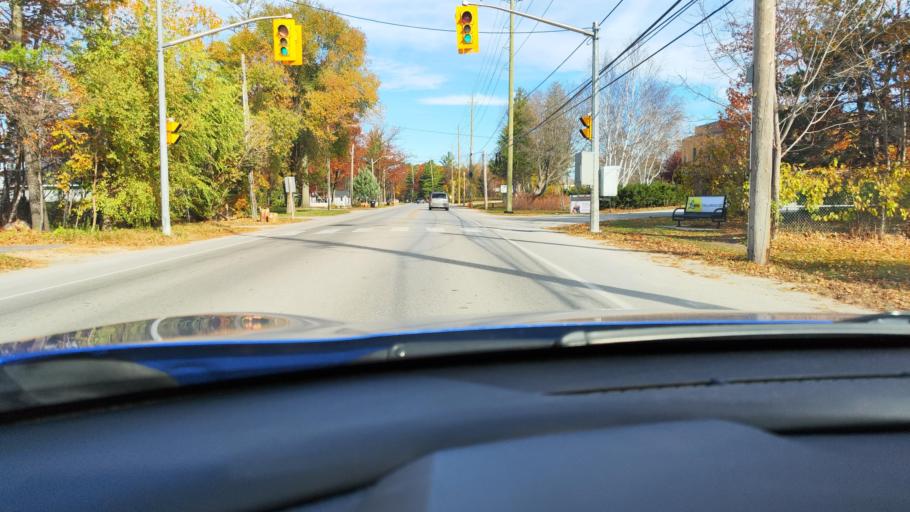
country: CA
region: Ontario
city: Wasaga Beach
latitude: 44.5112
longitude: -80.0261
